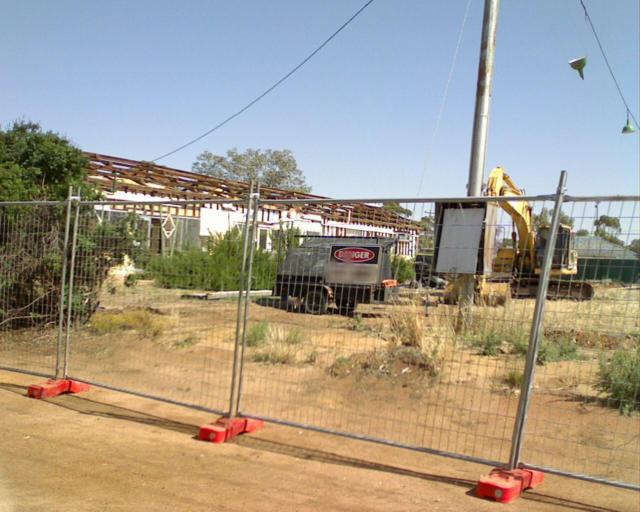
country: AU
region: Western Australia
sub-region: Merredin
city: Merredin
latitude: -30.9168
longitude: 118.2033
